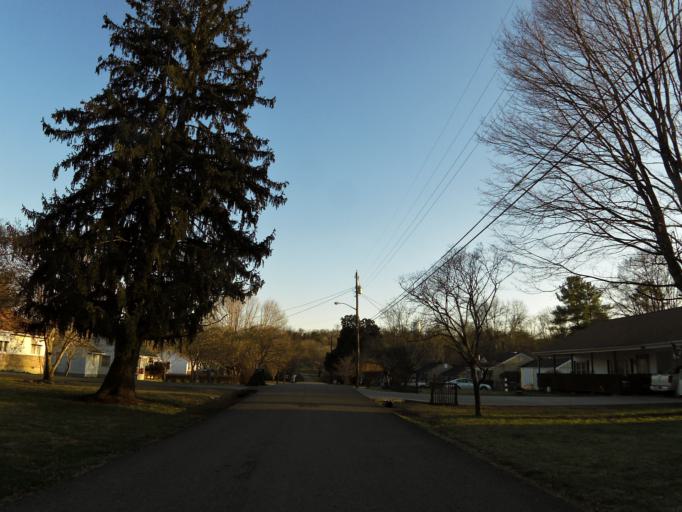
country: US
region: Tennessee
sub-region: Knox County
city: Knoxville
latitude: 36.0192
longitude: -83.8956
